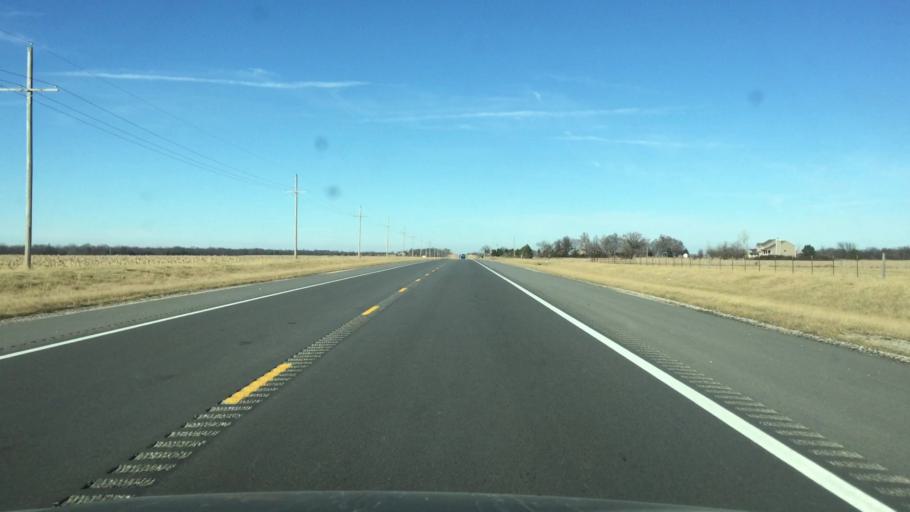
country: US
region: Kansas
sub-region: Franklin County
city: Ottawa
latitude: 38.5149
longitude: -95.2676
